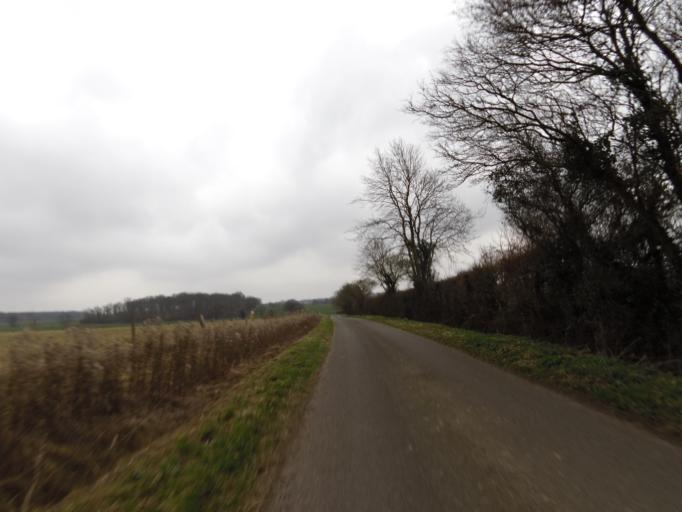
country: GB
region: England
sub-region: Suffolk
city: Framlingham
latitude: 52.1935
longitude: 1.3237
